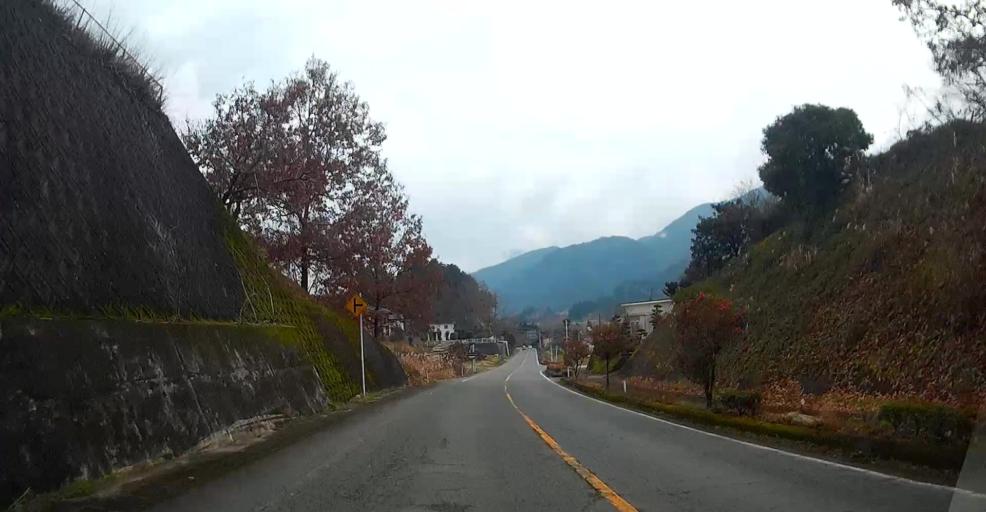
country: JP
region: Kumamoto
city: Matsubase
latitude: 32.6242
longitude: 130.8779
